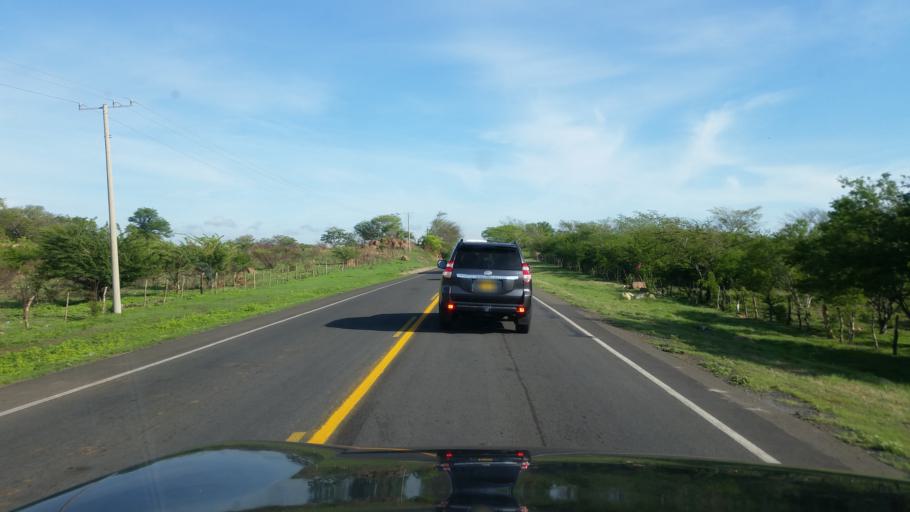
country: NI
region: Leon
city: La Paz Centro
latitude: 12.2263
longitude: -86.6984
